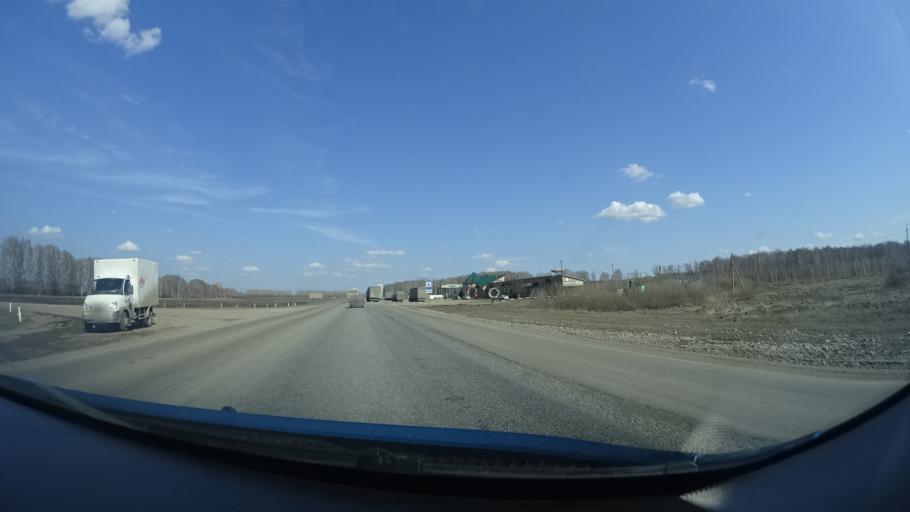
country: RU
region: Bashkortostan
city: Kandry
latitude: 54.6053
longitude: 54.3008
